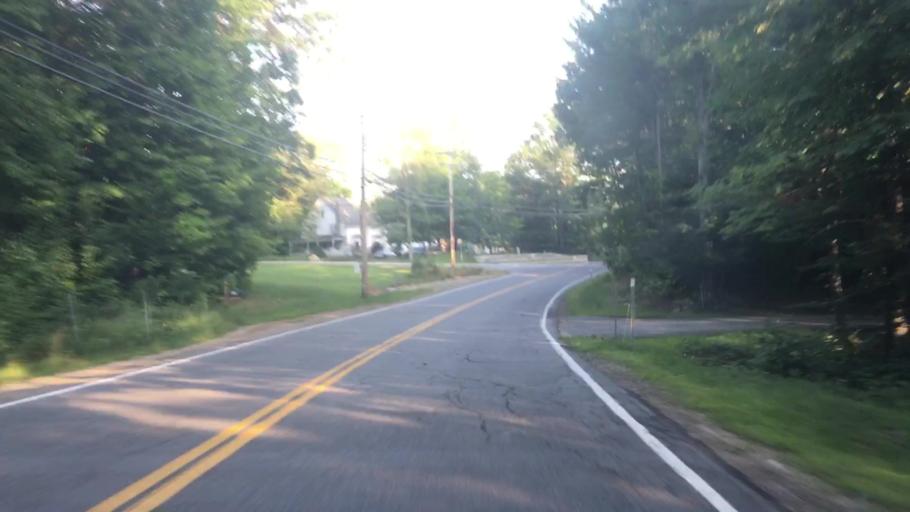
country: US
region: New Hampshire
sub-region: Belknap County
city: Laconia
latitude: 43.4934
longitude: -71.4391
